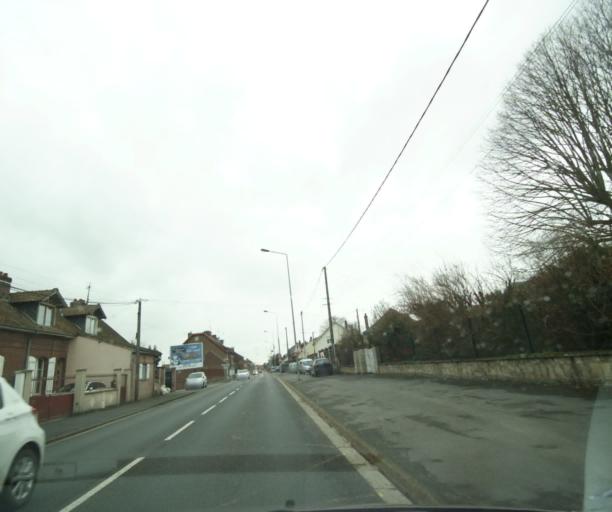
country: FR
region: Picardie
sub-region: Departement de l'Oise
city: Noyon
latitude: 49.5795
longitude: 3.0163
